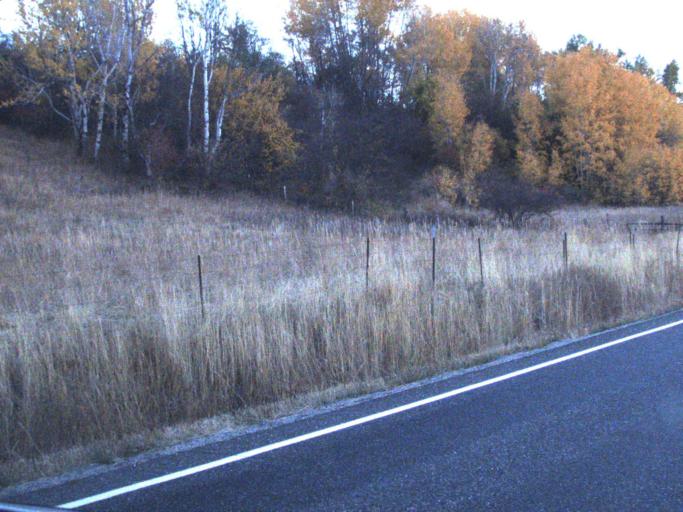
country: US
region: Washington
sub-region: Stevens County
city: Kettle Falls
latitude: 48.7407
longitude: -118.0489
